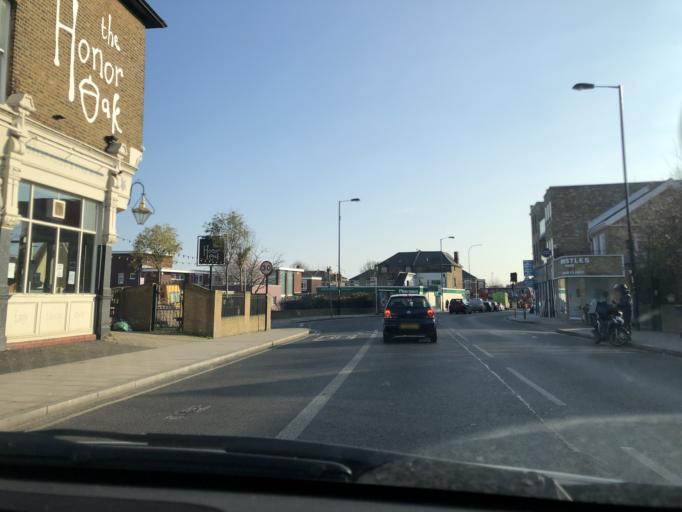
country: GB
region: England
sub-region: Greater London
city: Catford
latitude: 51.4434
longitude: -0.0425
